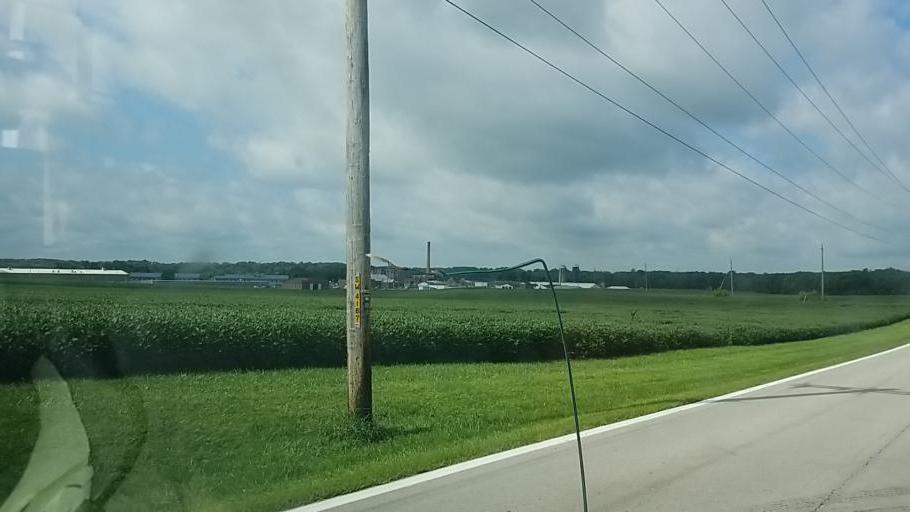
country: US
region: Ohio
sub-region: Franklin County
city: Grove City
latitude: 39.8030
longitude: -83.1535
